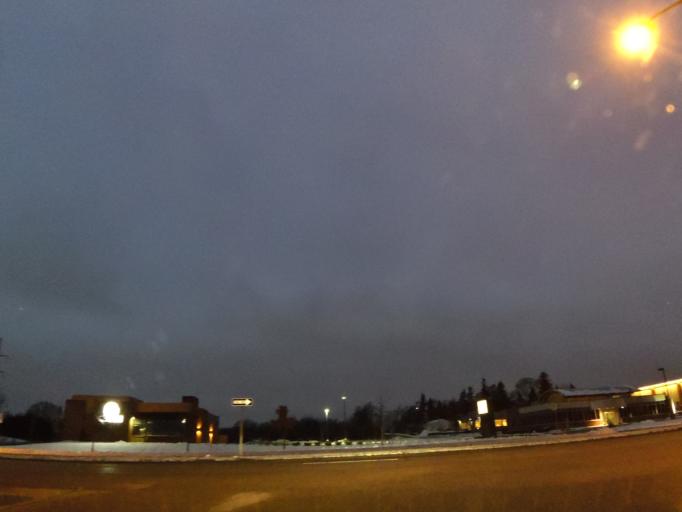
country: US
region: Minnesota
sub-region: Dakota County
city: Apple Valley
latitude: 44.6930
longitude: -93.2172
